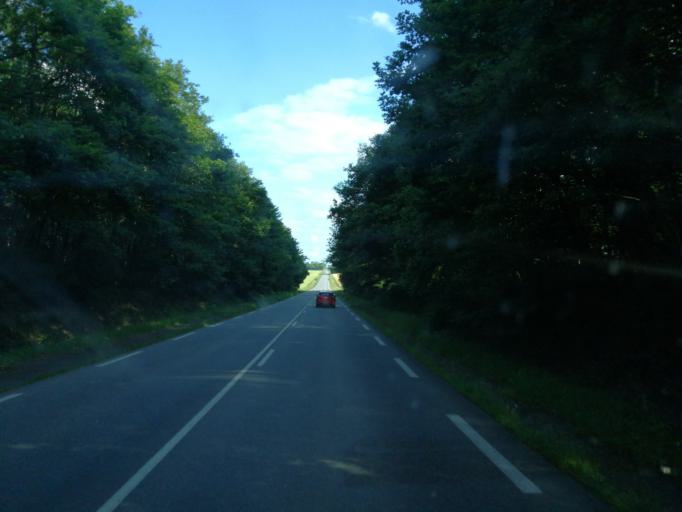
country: FR
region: Haute-Normandie
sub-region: Departement de l'Eure
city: Conches-en-Ouche
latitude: 49.0371
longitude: 0.9282
